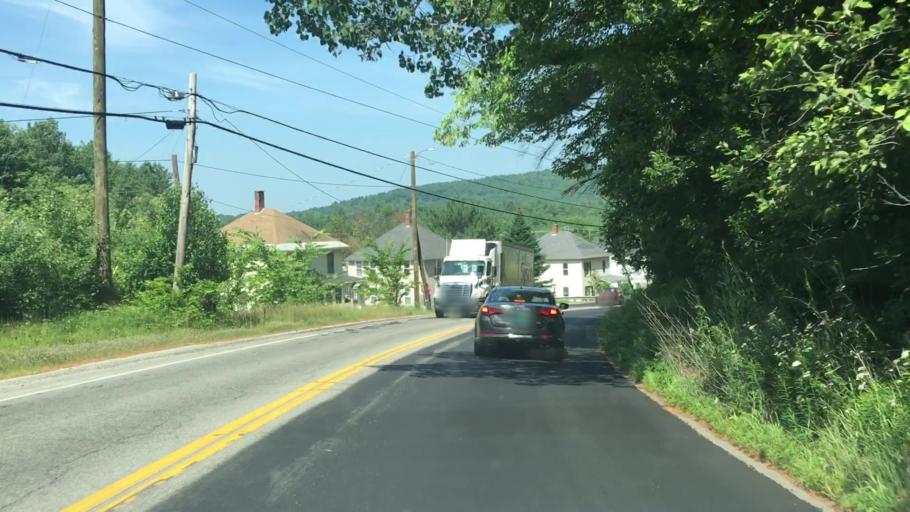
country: US
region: New Hampshire
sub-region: Sullivan County
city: Newport
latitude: 43.3746
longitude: -72.1356
